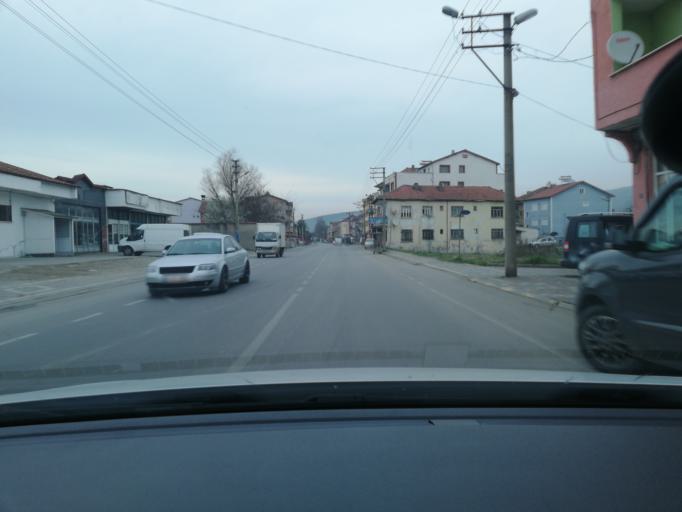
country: TR
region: Zonguldak
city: Caycuma
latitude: 41.4183
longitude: 32.0940
